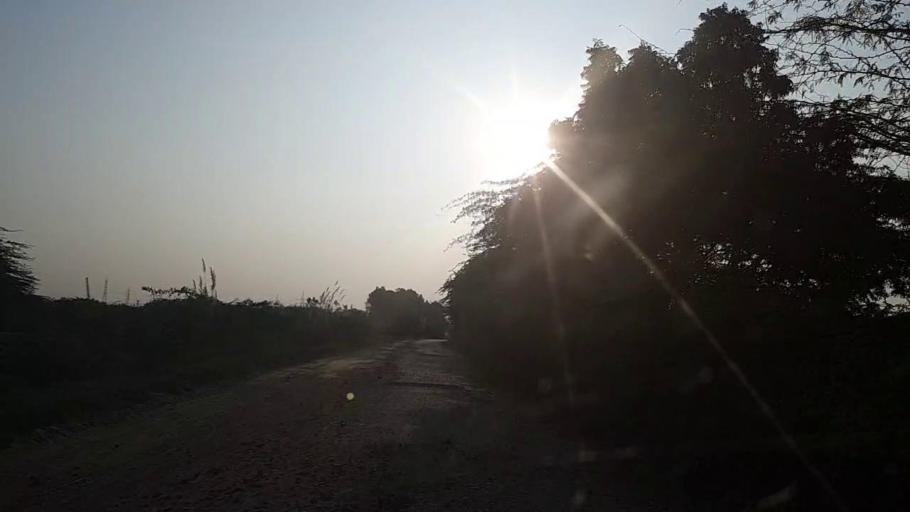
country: PK
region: Sindh
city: Mirpur Sakro
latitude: 24.5675
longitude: 67.6248
